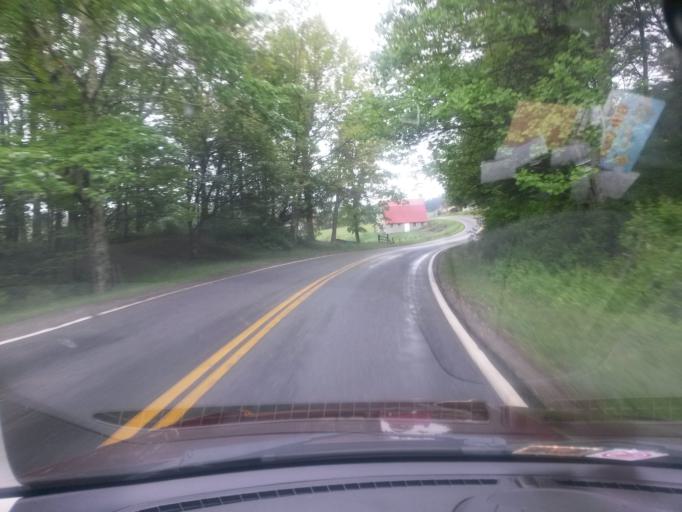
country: US
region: Virginia
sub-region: Patrick County
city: Stuart
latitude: 36.7545
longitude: -80.3912
